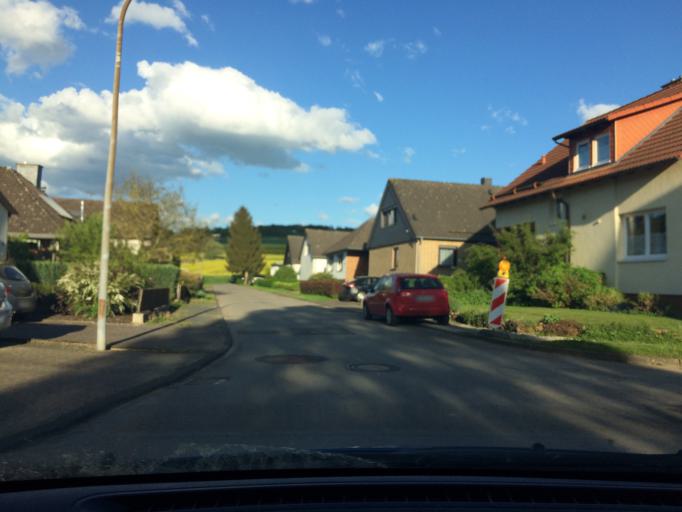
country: DE
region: Lower Saxony
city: Bodenfelde
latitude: 51.6175
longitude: 9.5568
